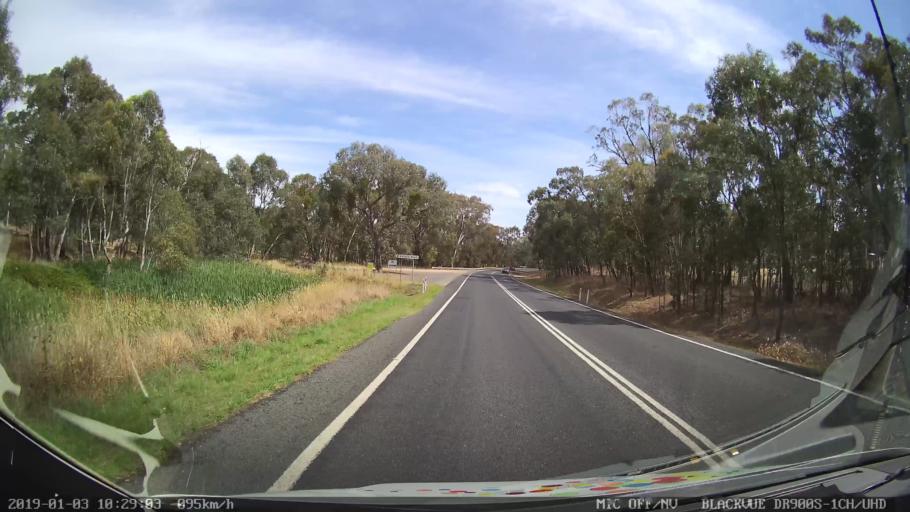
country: AU
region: New South Wales
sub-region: Young
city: Young
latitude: -34.3791
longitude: 148.2598
